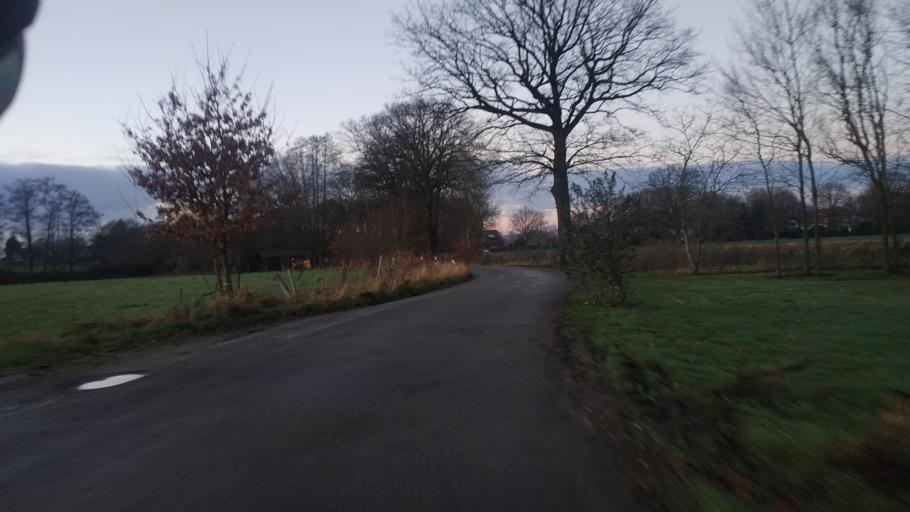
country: DE
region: North Rhine-Westphalia
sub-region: Regierungsbezirk Munster
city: Mettingen
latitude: 52.3199
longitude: 7.7633
